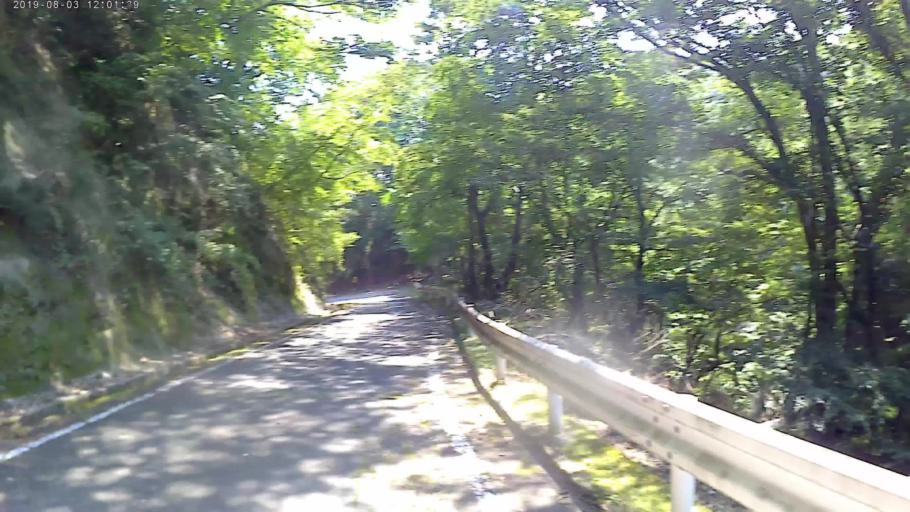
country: JP
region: Yamanashi
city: Enzan
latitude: 35.6130
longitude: 138.7835
